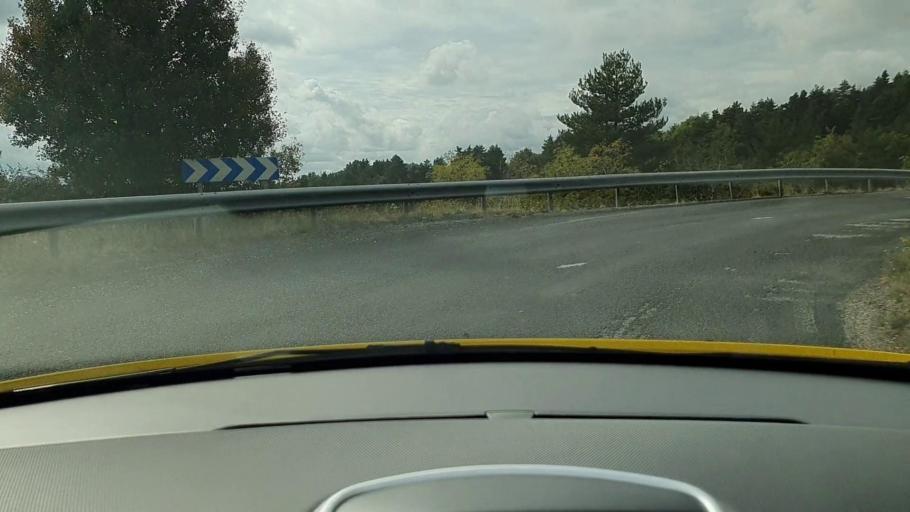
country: FR
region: Languedoc-Roussillon
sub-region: Departement de la Lozere
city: Meyrueis
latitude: 44.0651
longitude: 3.4115
